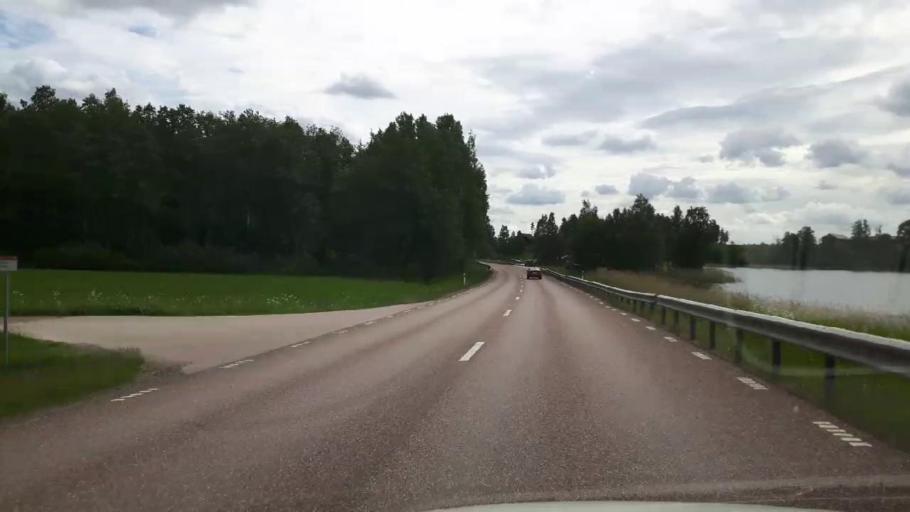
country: SE
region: Dalarna
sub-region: Hedemora Kommun
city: Hedemora
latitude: 60.3248
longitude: 15.9517
